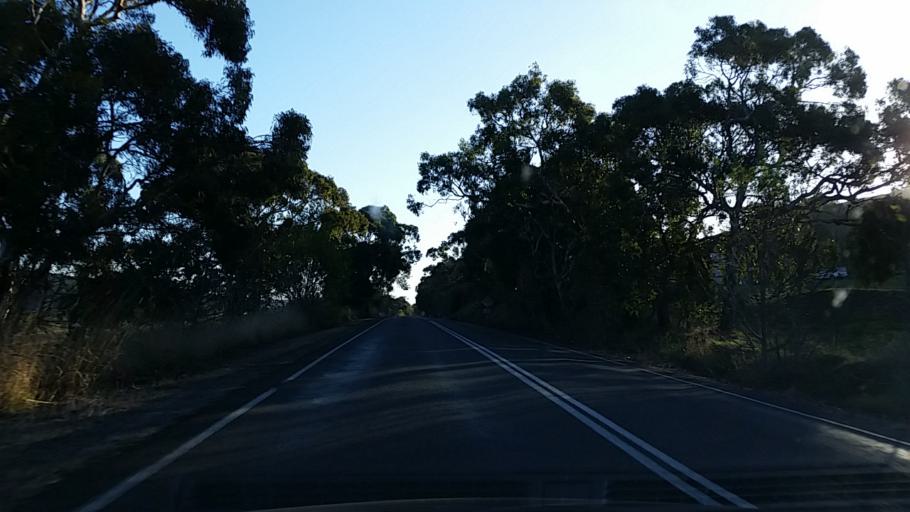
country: AU
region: South Australia
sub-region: Alexandrina
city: Mount Compass
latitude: -35.3481
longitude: 138.6425
